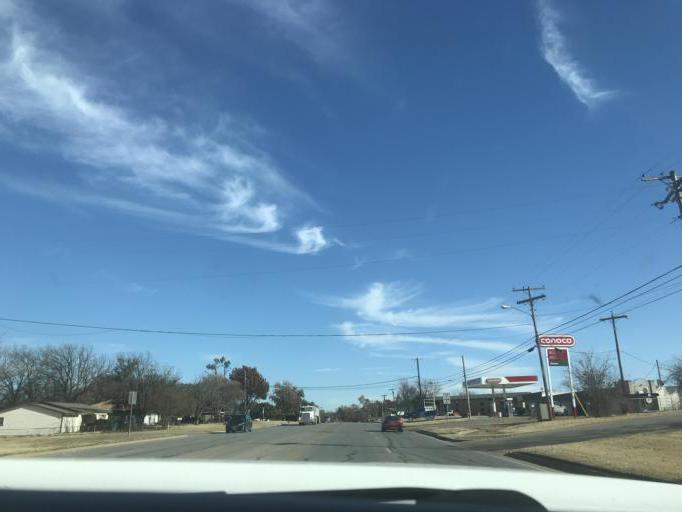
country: US
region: Texas
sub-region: Erath County
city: Stephenville
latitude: 32.2253
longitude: -98.2285
